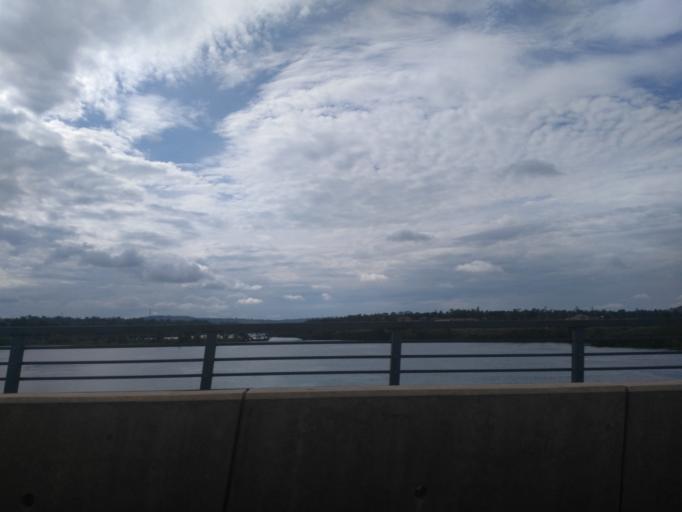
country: UG
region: Eastern Region
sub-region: Jinja District
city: Jinja
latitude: 0.4390
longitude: 33.1898
